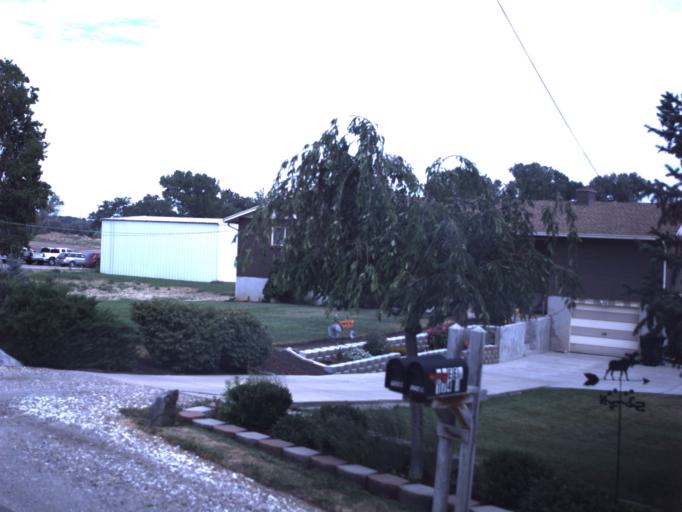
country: US
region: Utah
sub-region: Weber County
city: Washington Terrace
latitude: 41.1508
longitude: -111.9873
